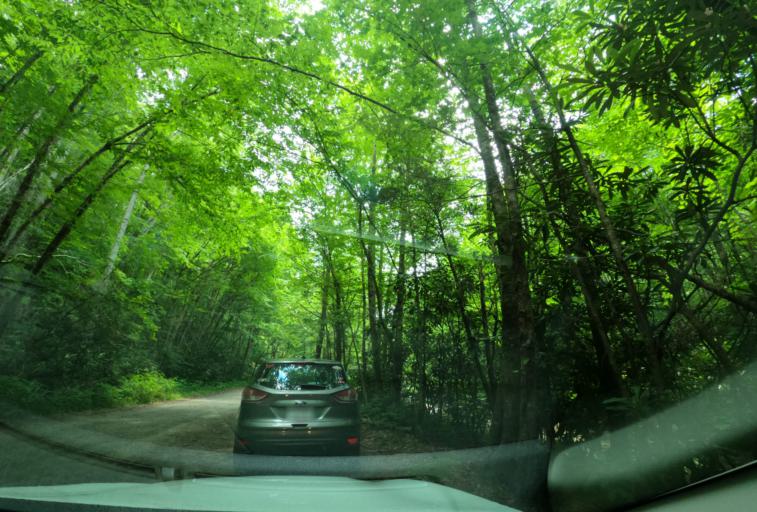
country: US
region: North Carolina
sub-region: Haywood County
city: Hazelwood
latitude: 35.3865
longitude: -82.8956
